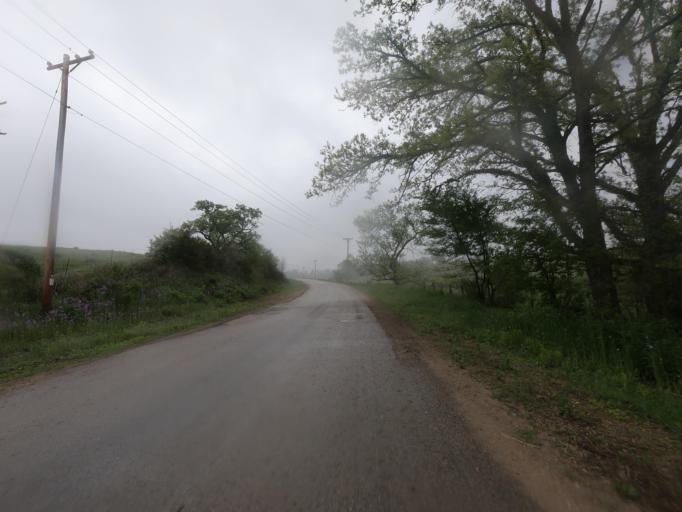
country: US
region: Wisconsin
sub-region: Grant County
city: Hazel Green
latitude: 42.5093
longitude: -90.4611
